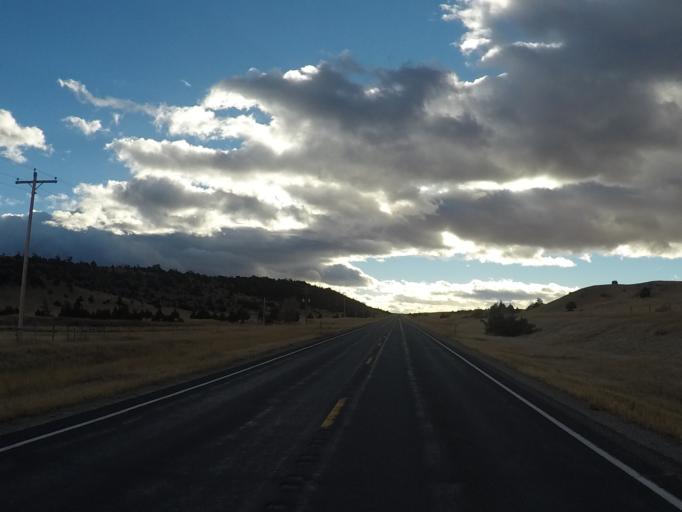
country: US
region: Montana
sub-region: Jefferson County
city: Whitehall
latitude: 45.9069
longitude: -111.9457
